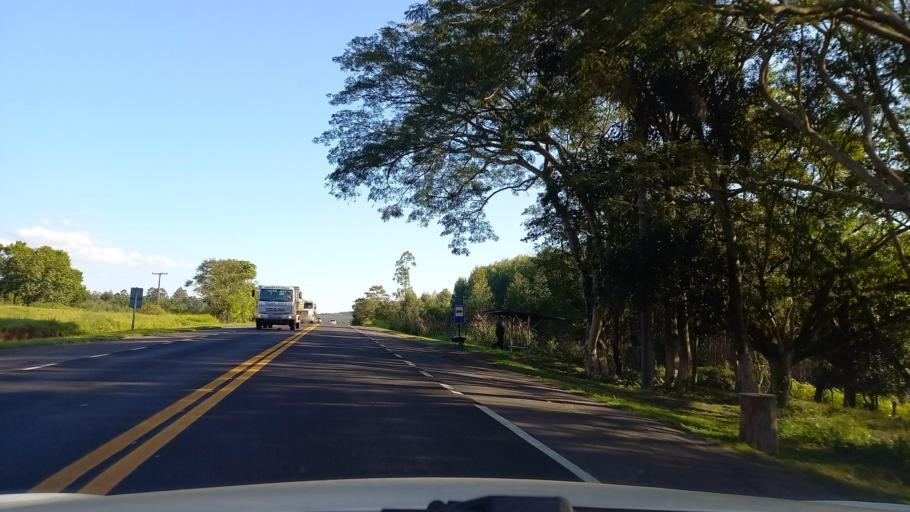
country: BR
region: Rio Grande do Sul
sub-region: Taquari
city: Taquari
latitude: -29.6938
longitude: -51.7471
